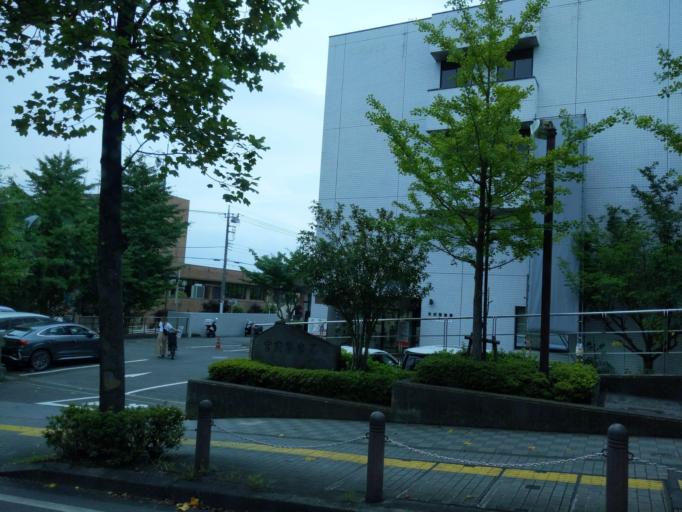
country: JP
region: Tokyo
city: Chofugaoka
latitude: 35.5885
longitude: 139.5785
